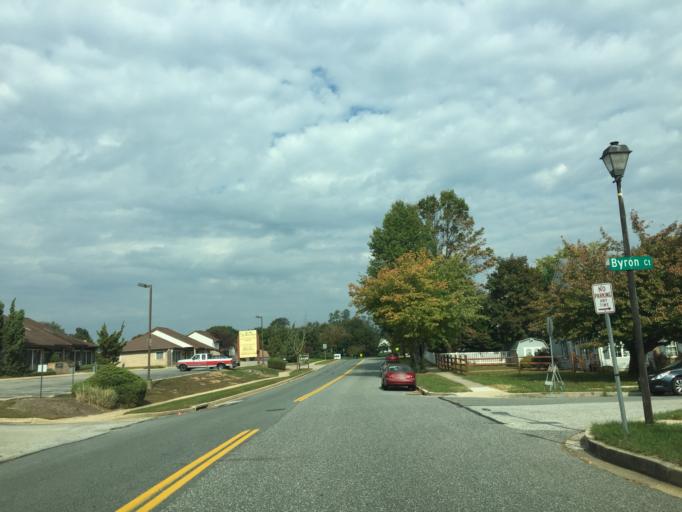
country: US
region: Maryland
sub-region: Harford County
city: Bel Air South
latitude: 39.4785
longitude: -76.3083
